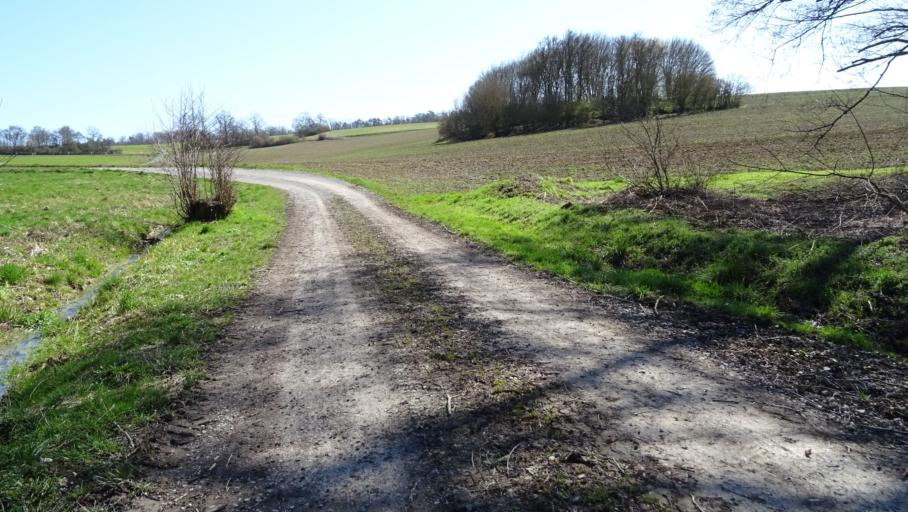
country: DE
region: Baden-Wuerttemberg
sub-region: Karlsruhe Region
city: Seckach
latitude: 49.4344
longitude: 9.3123
